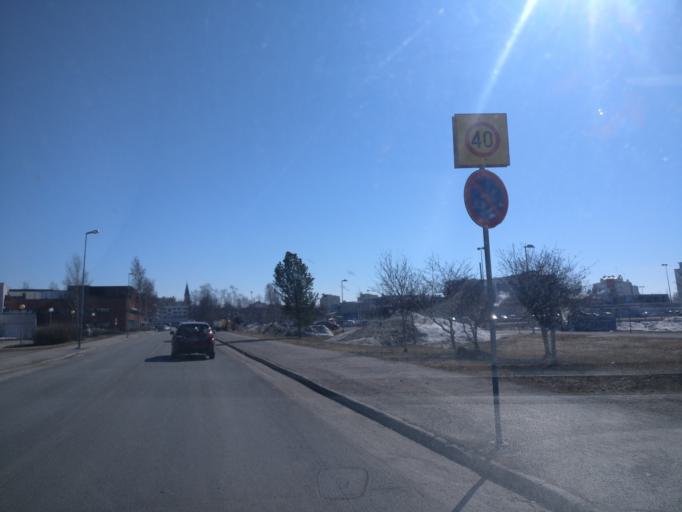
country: FI
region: Lapland
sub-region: Kemi-Tornio
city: Kemi
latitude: 65.7367
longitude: 24.5541
